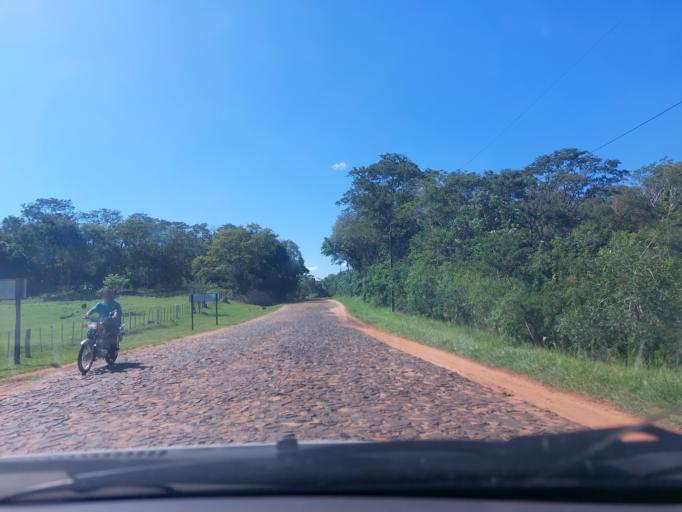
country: PY
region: San Pedro
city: Itacurubi del Rosario
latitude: -24.5666
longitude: -56.5946
